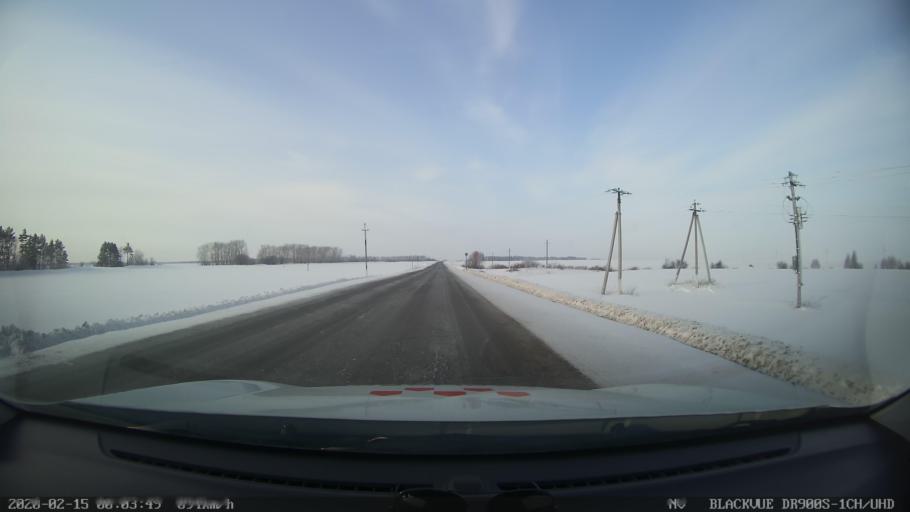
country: RU
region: Tatarstan
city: Kuybyshevskiy Zaton
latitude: 55.3760
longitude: 48.9923
